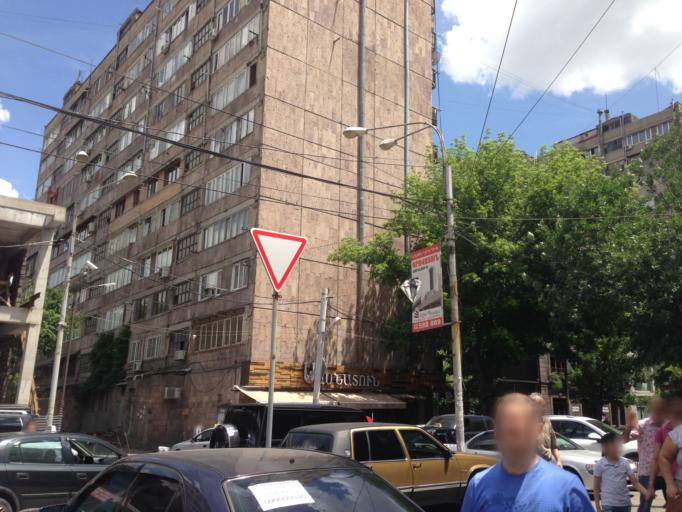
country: AM
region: Yerevan
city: Yerevan
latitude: 40.1733
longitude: 44.5106
